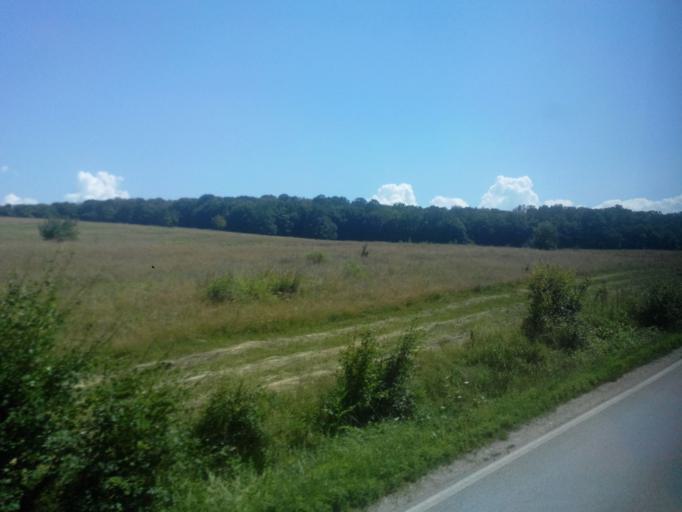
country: RO
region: Hunedoara
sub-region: Comuna Dobra
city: Dobra
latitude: 45.9145
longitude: 22.5480
